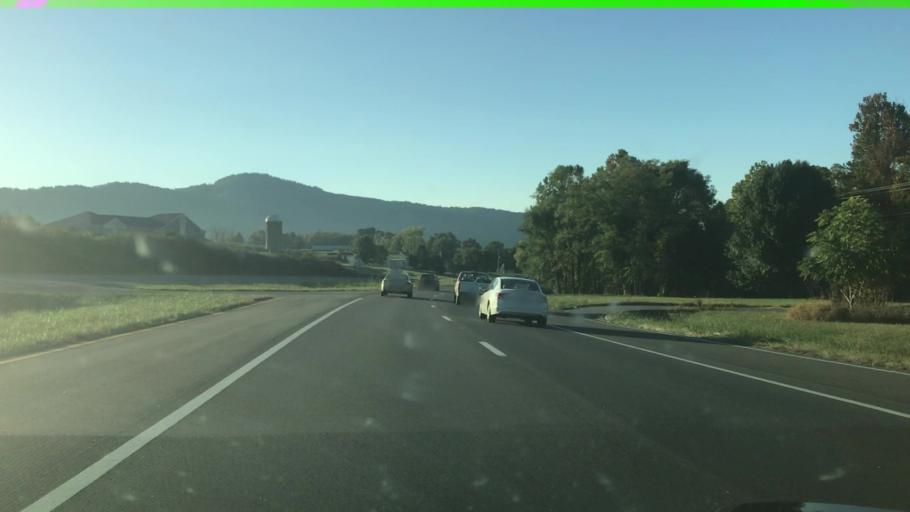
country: US
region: Virginia
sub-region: Botetourt County
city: Laymantown
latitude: 37.3409
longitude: -79.8765
